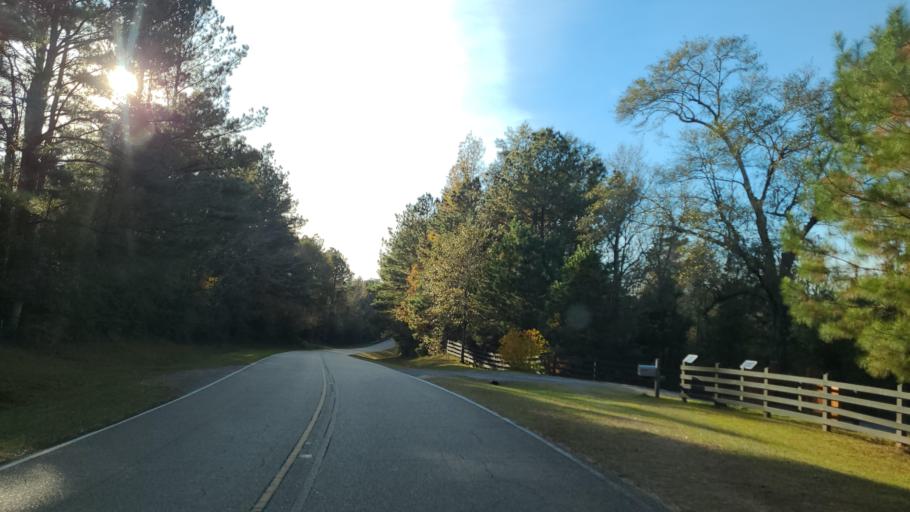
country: US
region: Mississippi
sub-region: Lamar County
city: Purvis
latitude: 31.1663
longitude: -89.3198
